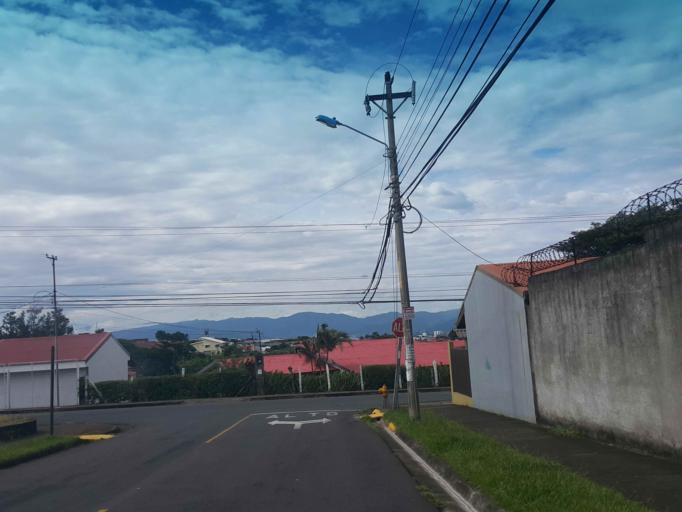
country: CR
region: Heredia
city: Heredia
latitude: 10.0089
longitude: -84.1204
